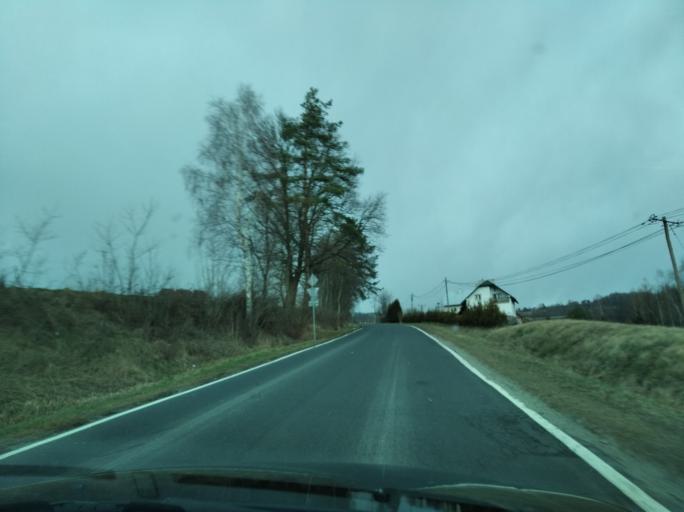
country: PL
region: Subcarpathian Voivodeship
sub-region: Powiat rzeszowski
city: Hyzne
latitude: 49.9120
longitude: 22.1997
